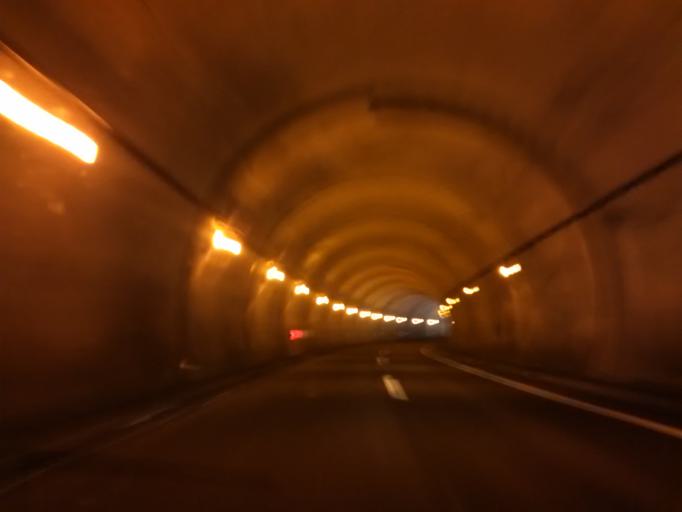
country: ES
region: Asturias
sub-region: Province of Asturias
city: Pola de Lena
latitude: 43.0108
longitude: -5.8171
